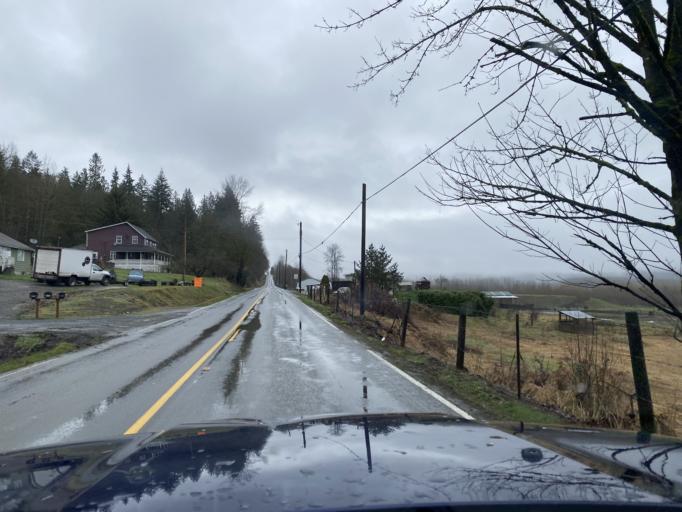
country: US
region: Washington
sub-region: King County
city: Duvall
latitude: 47.7759
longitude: -122.0002
